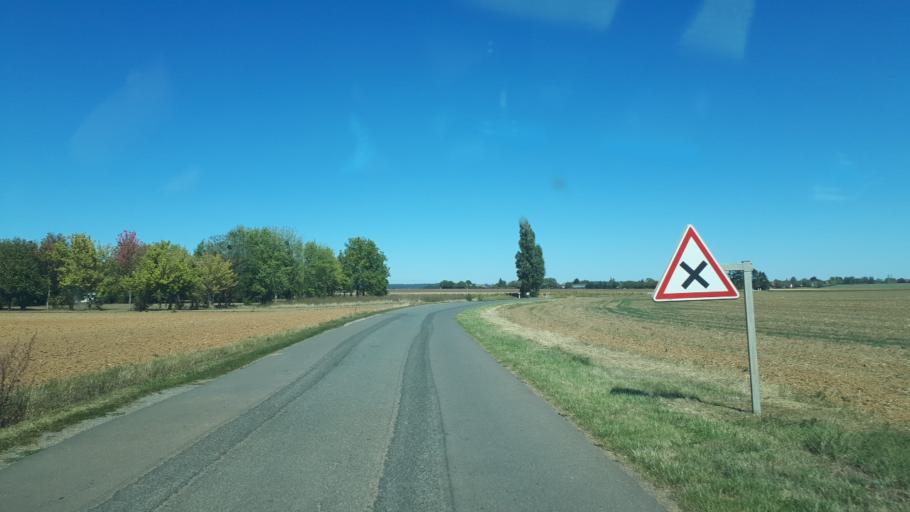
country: FR
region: Centre
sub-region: Departement du Cher
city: Rians
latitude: 47.1944
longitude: 2.7165
